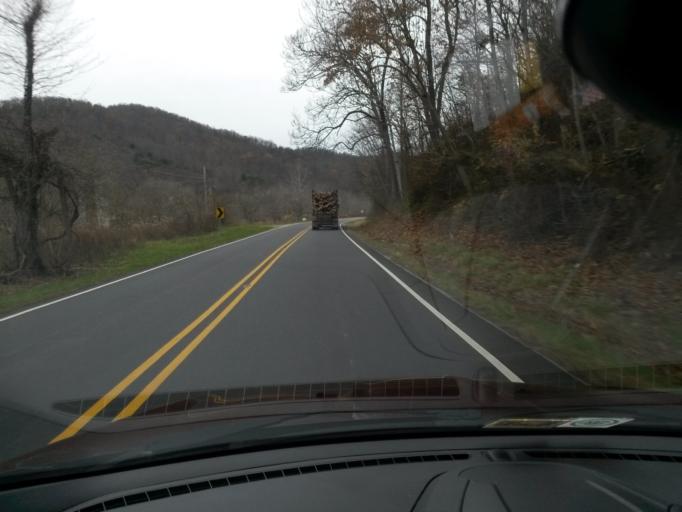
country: US
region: Virginia
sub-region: City of Buena Vista
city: Buena Vista
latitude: 37.6694
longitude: -79.2134
